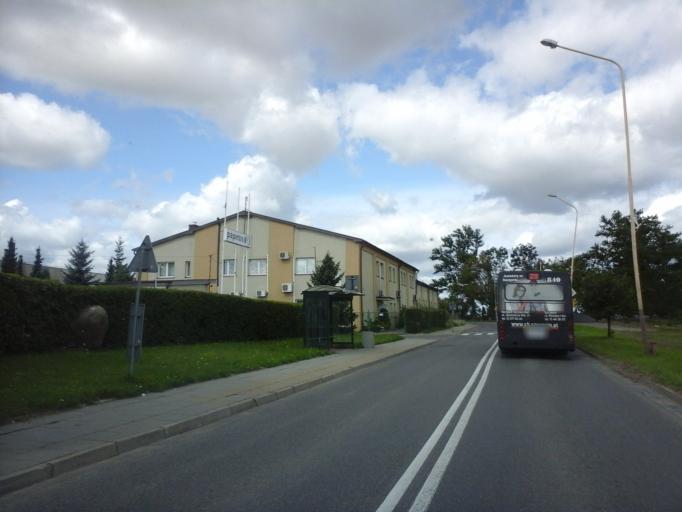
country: PL
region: West Pomeranian Voivodeship
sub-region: Powiat pyrzycki
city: Warnice
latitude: 53.3002
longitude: 15.0055
